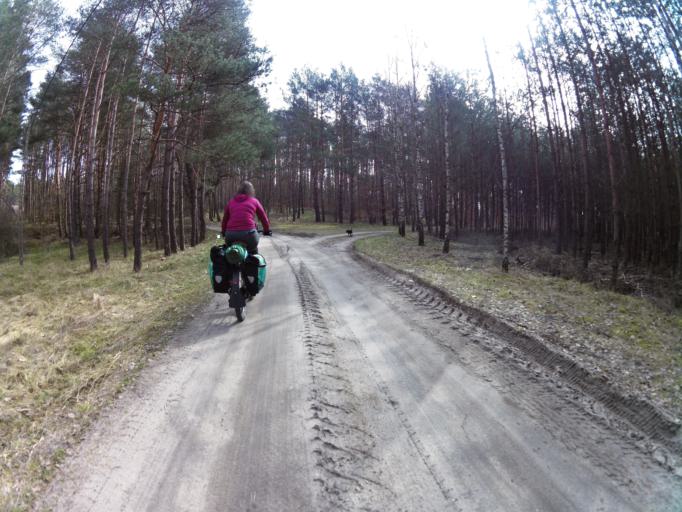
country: PL
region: West Pomeranian Voivodeship
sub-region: Powiat mysliborski
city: Mysliborz
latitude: 52.8554
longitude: 14.8373
